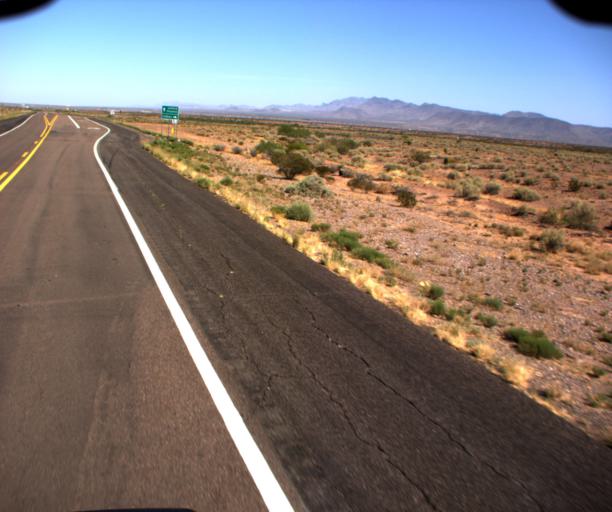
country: US
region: Arizona
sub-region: Graham County
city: Safford
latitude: 32.7904
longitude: -109.5485
